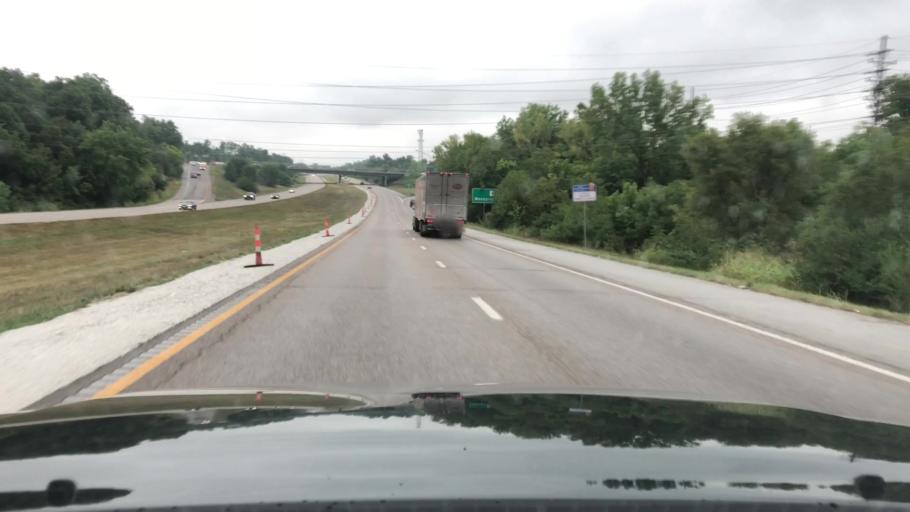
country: US
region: Missouri
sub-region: Saint Charles County
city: Wentzville
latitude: 38.8268
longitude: -90.8524
